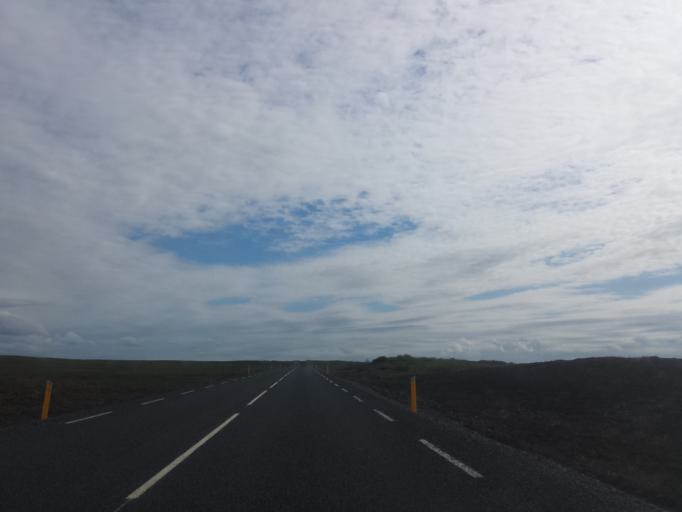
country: IS
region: Northeast
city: Husavik
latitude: 65.9934
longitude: -16.5653
